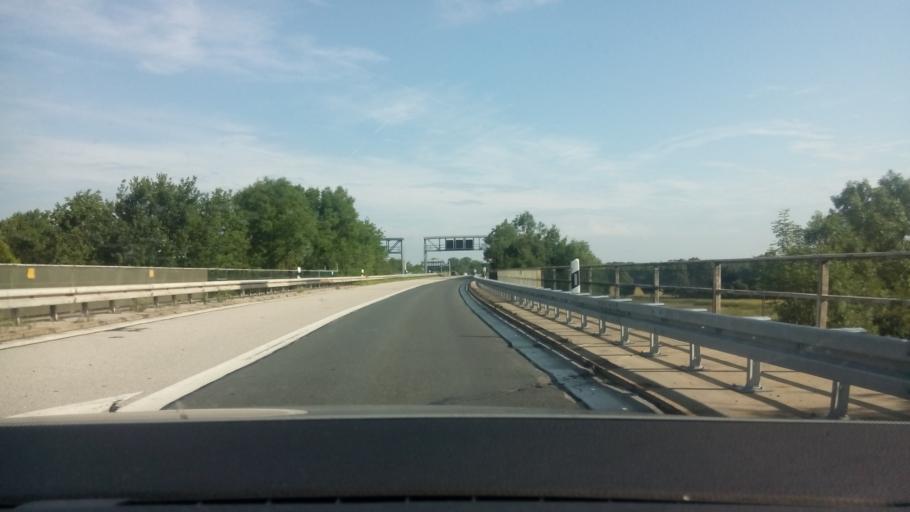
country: DE
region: Bavaria
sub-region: Upper Bavaria
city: Oberschleissheim
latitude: 48.2286
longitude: 11.5438
